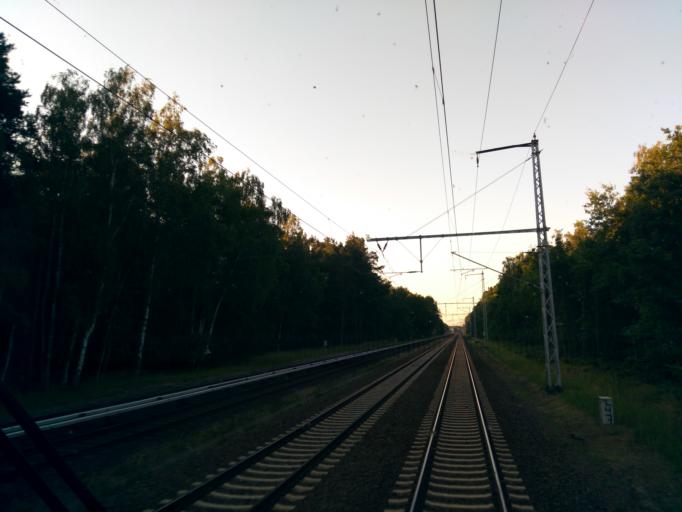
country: DE
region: Brandenburg
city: Zeuthen
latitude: 52.3822
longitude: 13.6081
